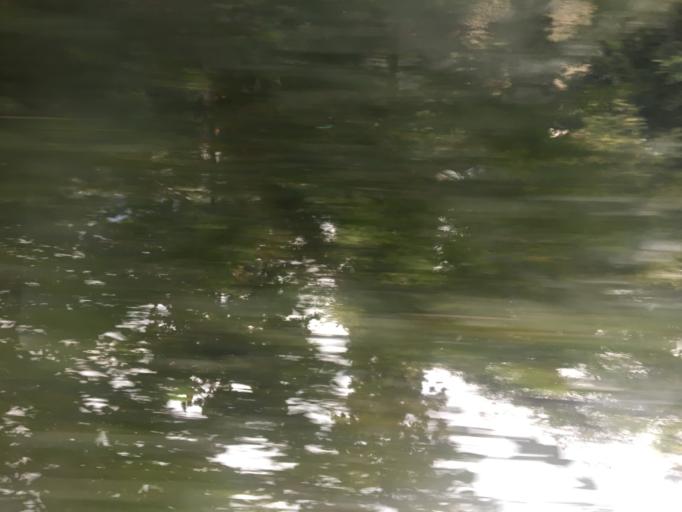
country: JP
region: Saitama
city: Hanno
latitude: 35.8402
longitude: 139.3342
